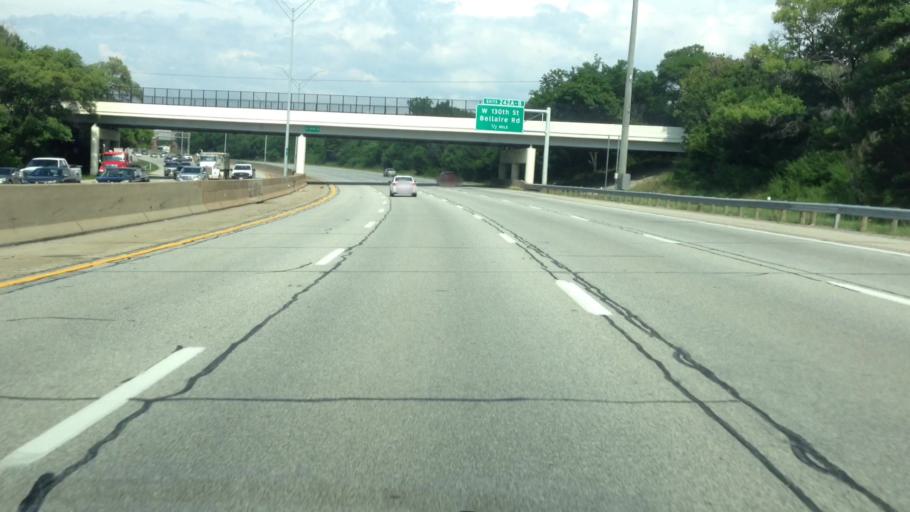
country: US
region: Ohio
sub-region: Cuyahoga County
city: Brook Park
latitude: 41.4387
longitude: -81.7919
